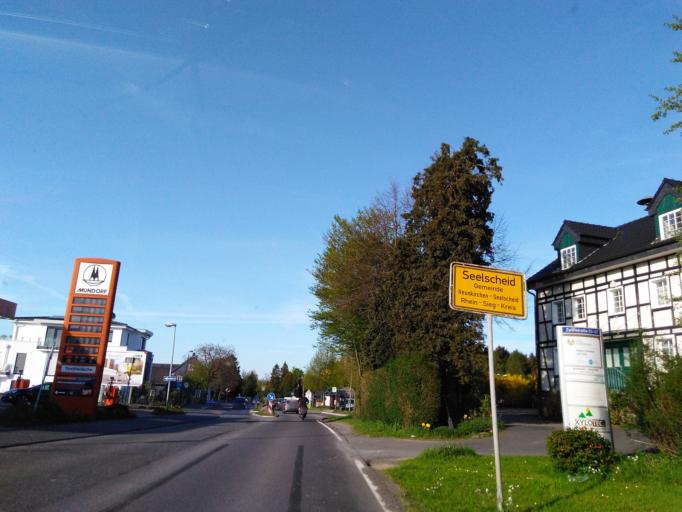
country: DE
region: North Rhine-Westphalia
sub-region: Regierungsbezirk Koln
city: Overath
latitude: 50.8652
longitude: 7.3170
